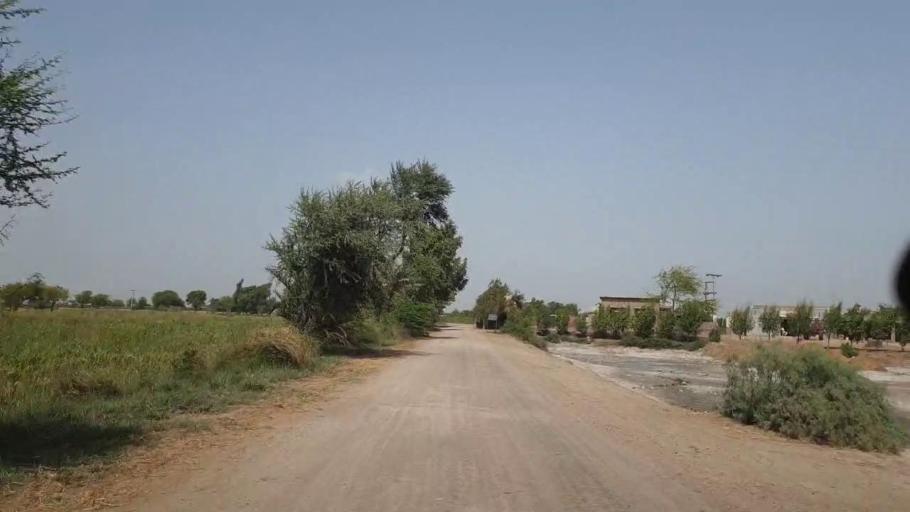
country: PK
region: Sindh
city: Matli
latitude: 25.0729
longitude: 68.7073
